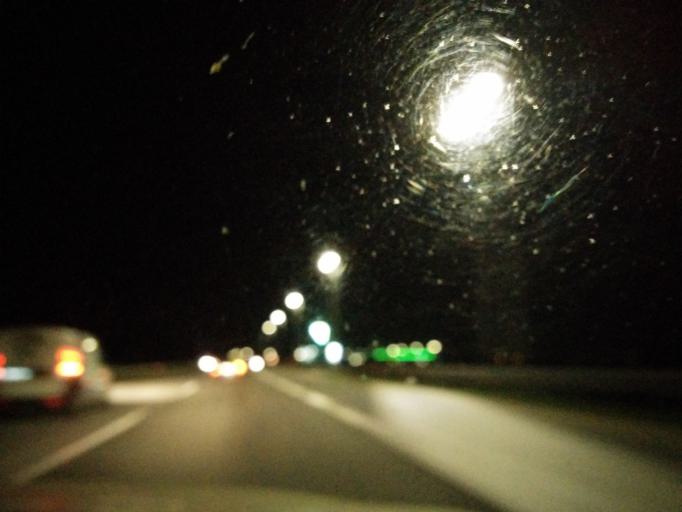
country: RS
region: Autonomna Pokrajina Vojvodina
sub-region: Sremski Okrug
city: Pecinci
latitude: 44.9330
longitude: 19.9189
